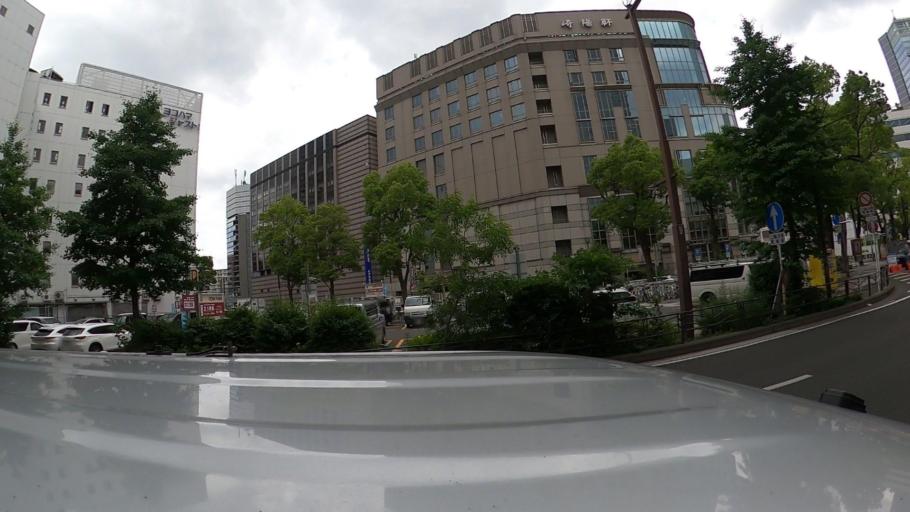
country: JP
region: Kanagawa
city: Yokohama
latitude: 35.4636
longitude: 139.6237
